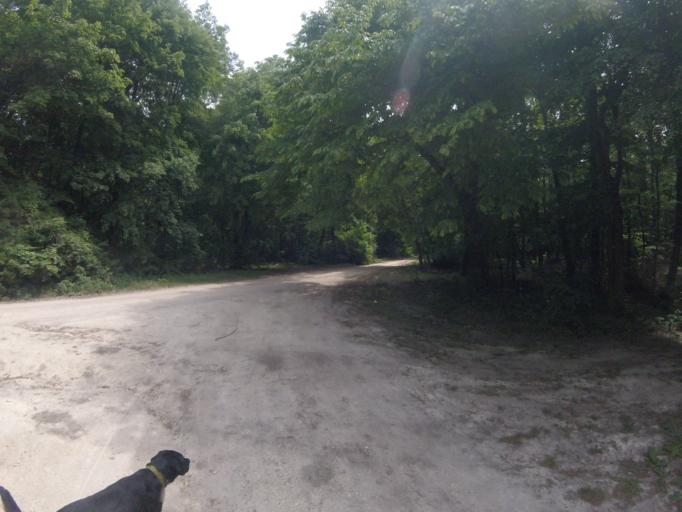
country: HU
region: Pest
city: Telki
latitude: 47.5632
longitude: 18.8493
